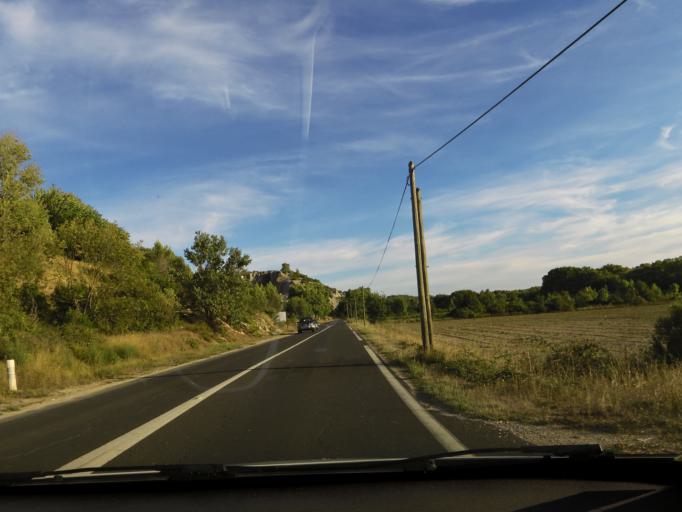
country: FR
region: Languedoc-Roussillon
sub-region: Departement de l'Herault
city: Prades-le-Lez
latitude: 43.7112
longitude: 3.8672
